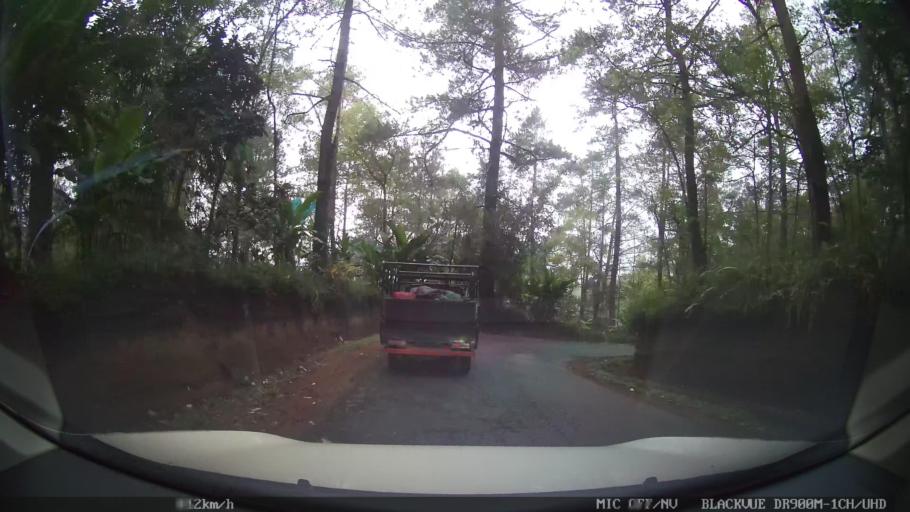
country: ID
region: Bali
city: Banjar Kedisan
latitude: -8.2634
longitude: 115.3337
